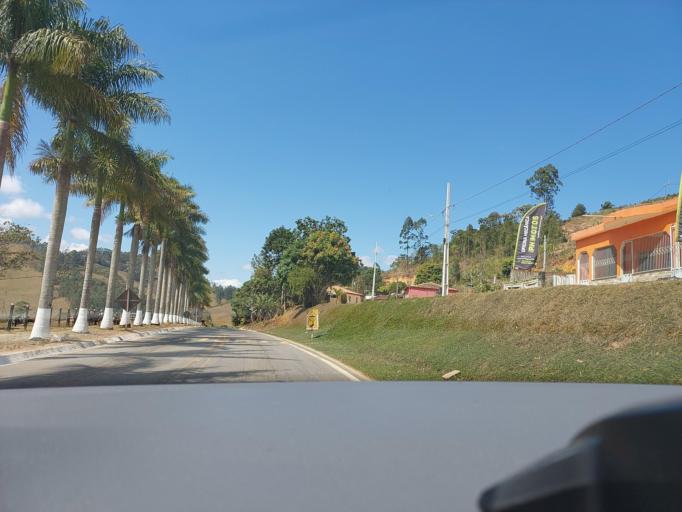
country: BR
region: Minas Gerais
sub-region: Mirai
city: Mirai
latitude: -21.0132
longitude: -42.5455
